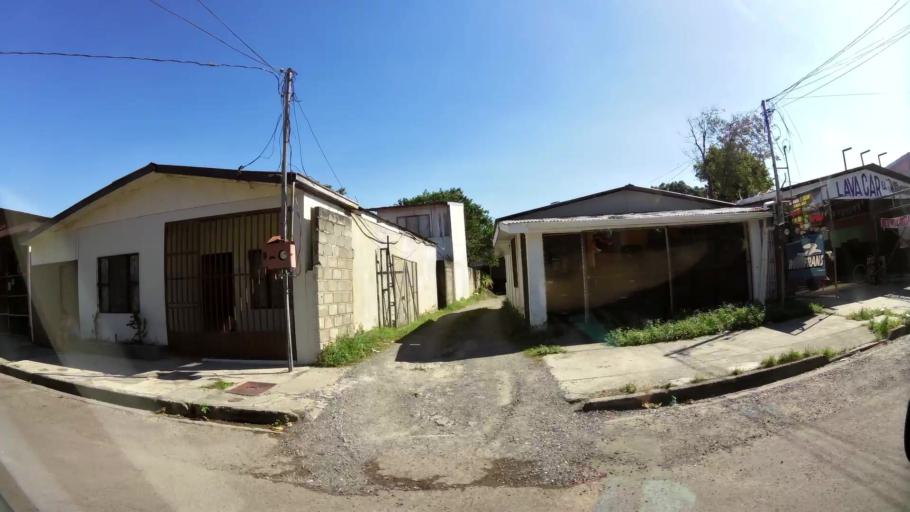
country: CR
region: Guanacaste
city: Liberia
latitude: 10.6324
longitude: -85.4414
